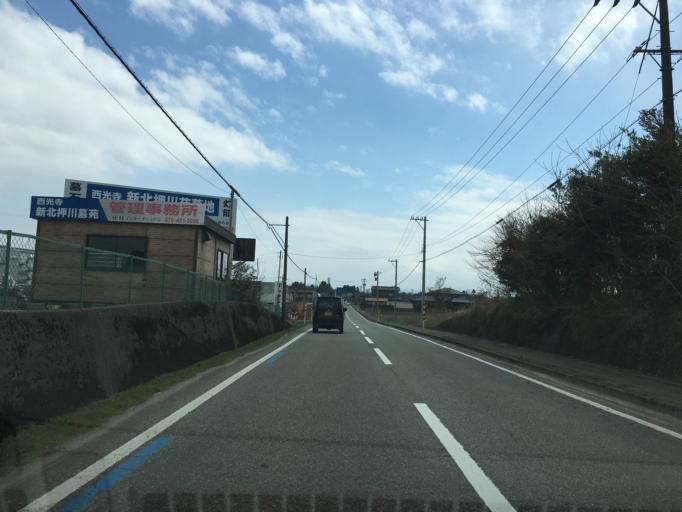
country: JP
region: Toyama
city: Kuragaki-kosugi
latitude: 36.6784
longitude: 137.1240
